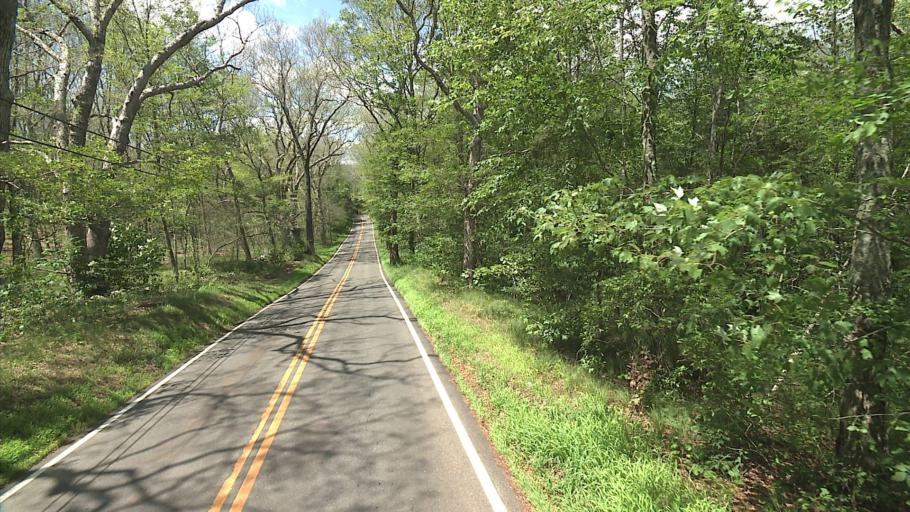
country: US
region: Connecticut
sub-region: Middlesex County
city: Essex Village
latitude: 41.4459
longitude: -72.3369
